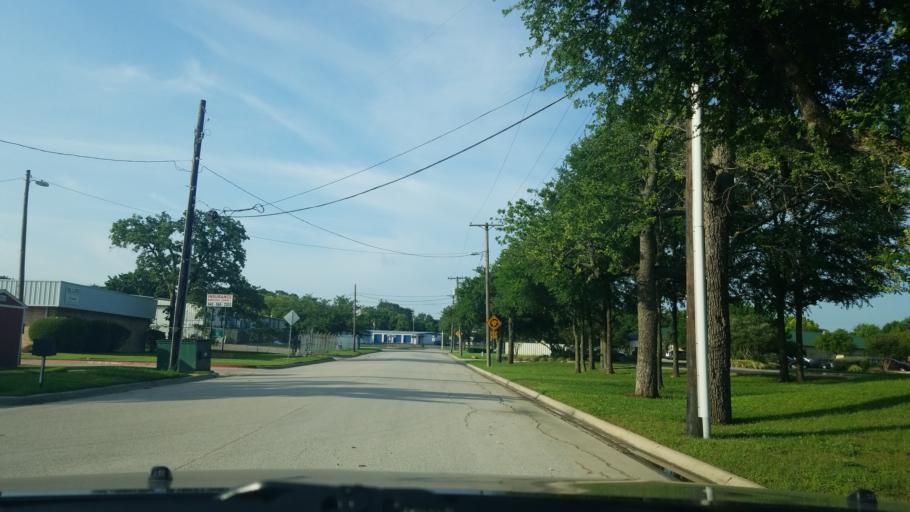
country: US
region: Texas
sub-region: Denton County
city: Denton
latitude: 33.2018
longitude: -97.1214
